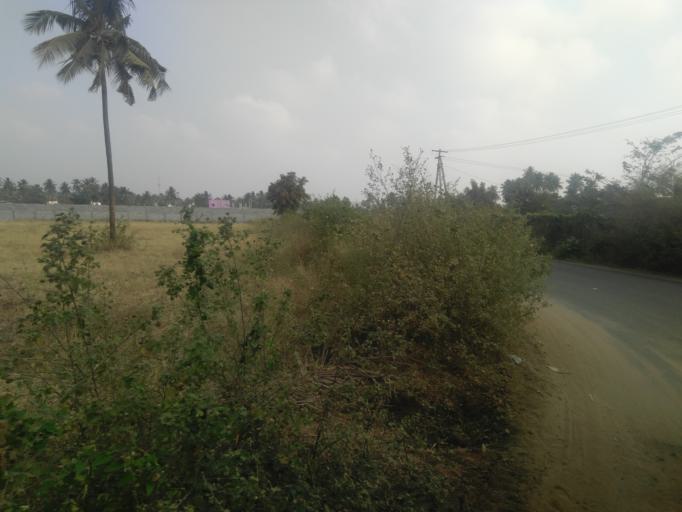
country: IN
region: Tamil Nadu
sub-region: Coimbatore
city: Coimbatore
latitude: 11.0711
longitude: 76.9204
